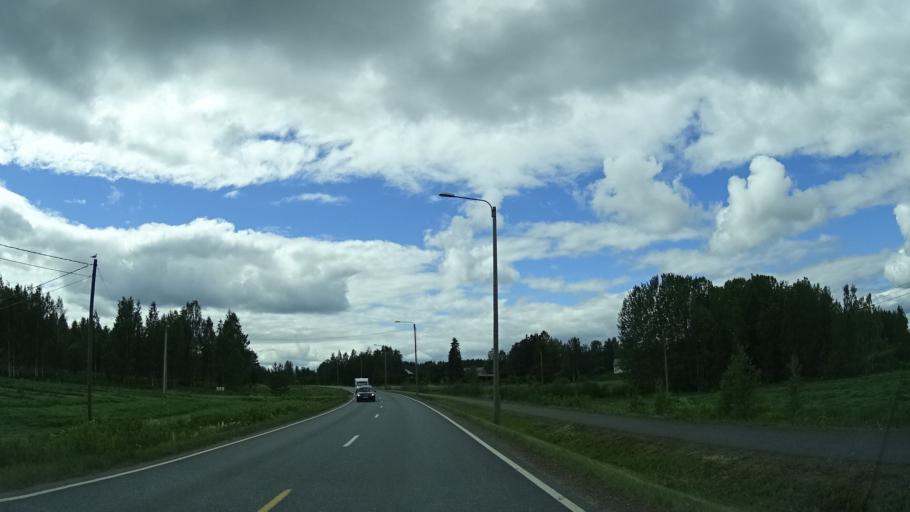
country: FI
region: Central Finland
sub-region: Joutsa
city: Luhanka
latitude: 61.8360
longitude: 25.8517
